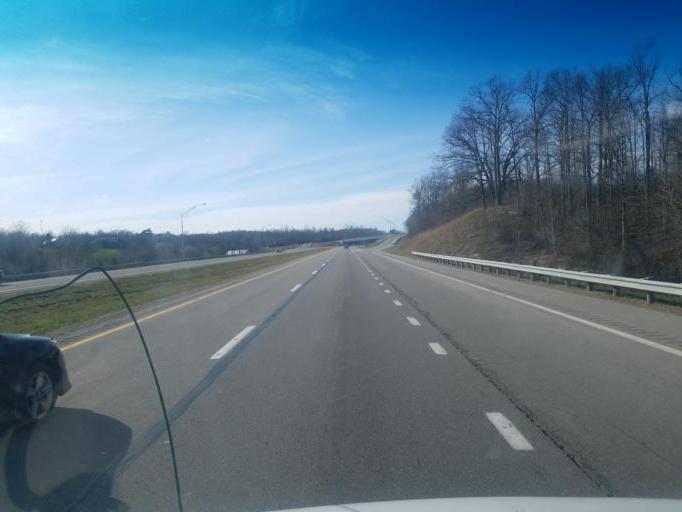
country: US
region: Ohio
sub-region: Logan County
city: Bellefontaine
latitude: 40.3381
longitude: -83.6896
